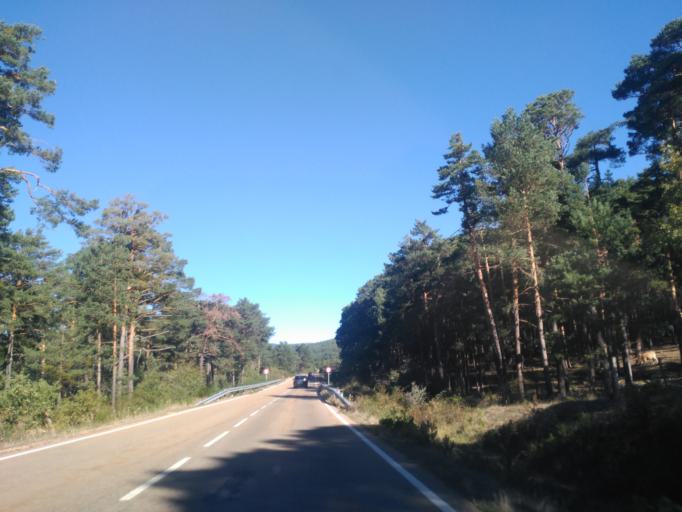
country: ES
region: Castille and Leon
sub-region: Provincia de Soria
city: Vinuesa
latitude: 41.9373
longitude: -2.7673
